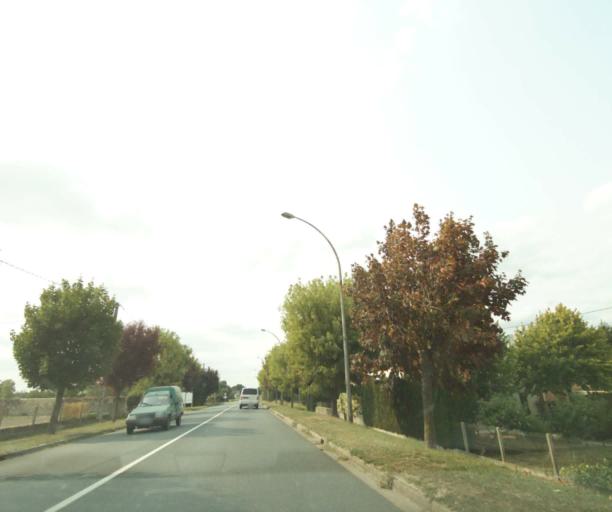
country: FR
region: Centre
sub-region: Departement de l'Indre
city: Chatillon-sur-Indre
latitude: 46.9964
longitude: 1.1577
